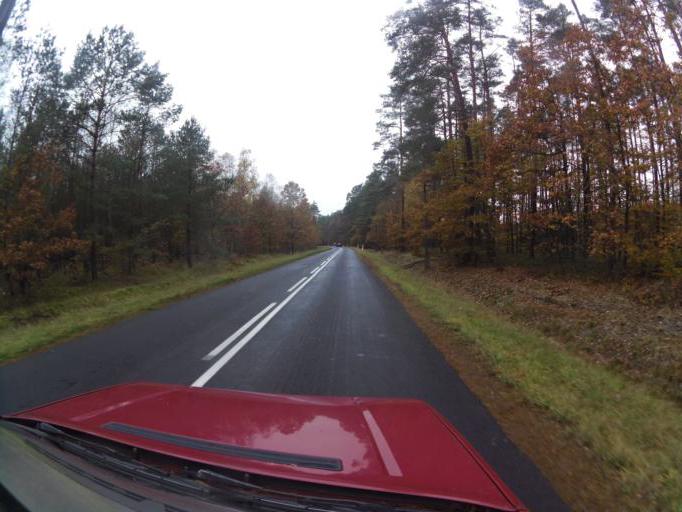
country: PL
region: West Pomeranian Voivodeship
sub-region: Powiat policki
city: Dobra
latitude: 53.5886
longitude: 14.3726
